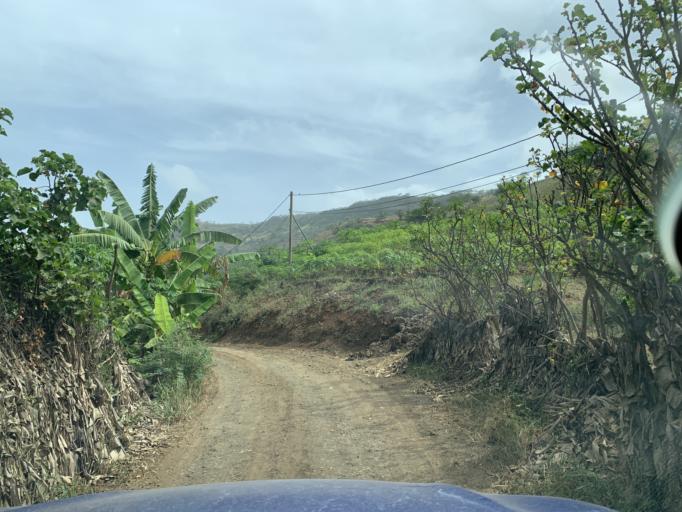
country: CV
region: Santa Cruz
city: Santa Cruz
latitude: 15.1110
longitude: -23.5617
